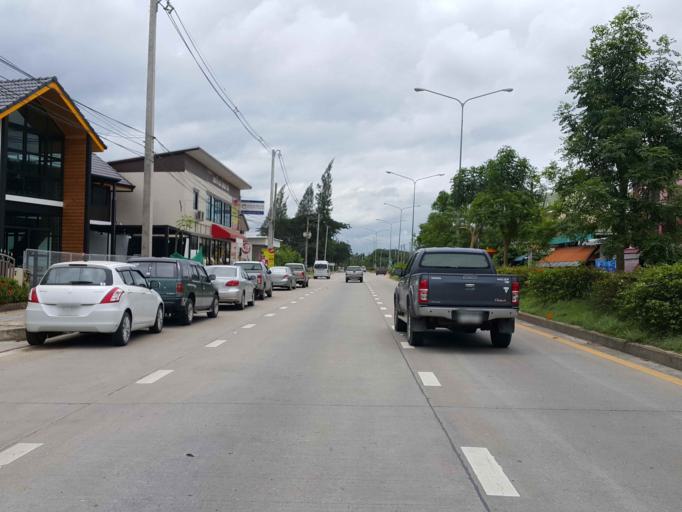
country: TH
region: Chiang Mai
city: San Sai
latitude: 18.8334
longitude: 99.0036
